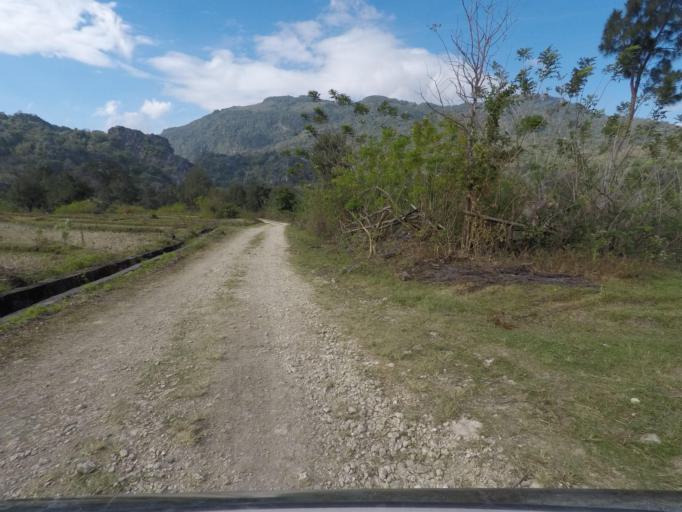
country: TL
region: Baucau
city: Venilale
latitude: -8.6554
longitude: 126.3948
